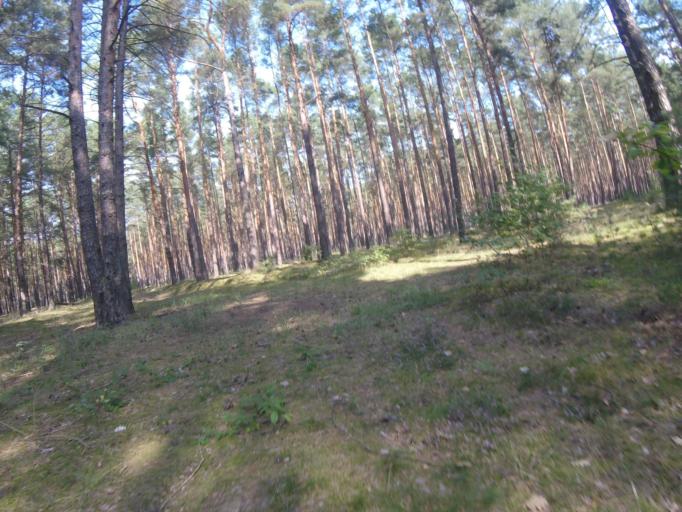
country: DE
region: Brandenburg
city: Bestensee
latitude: 52.2821
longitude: 13.7159
